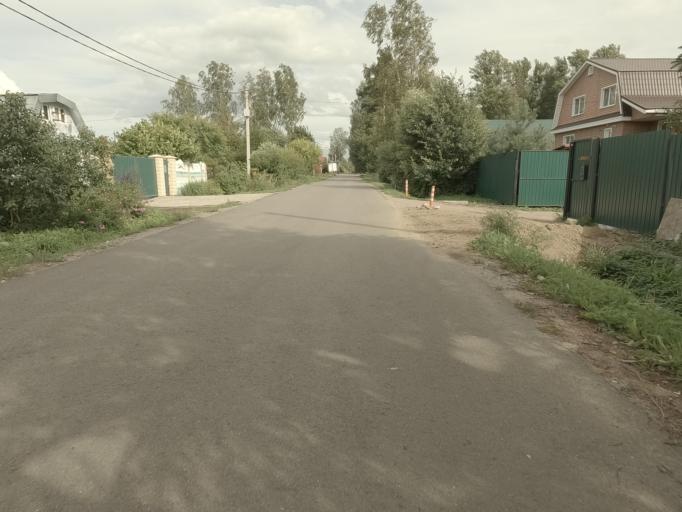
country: RU
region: Leningrad
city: Mga
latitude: 59.7589
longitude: 31.0442
